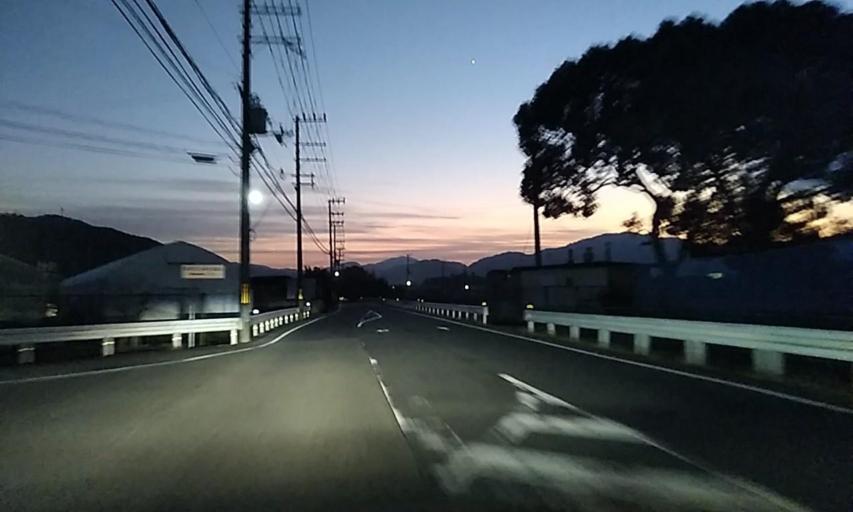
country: JP
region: Kyoto
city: Kameoka
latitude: 35.0154
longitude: 135.5636
